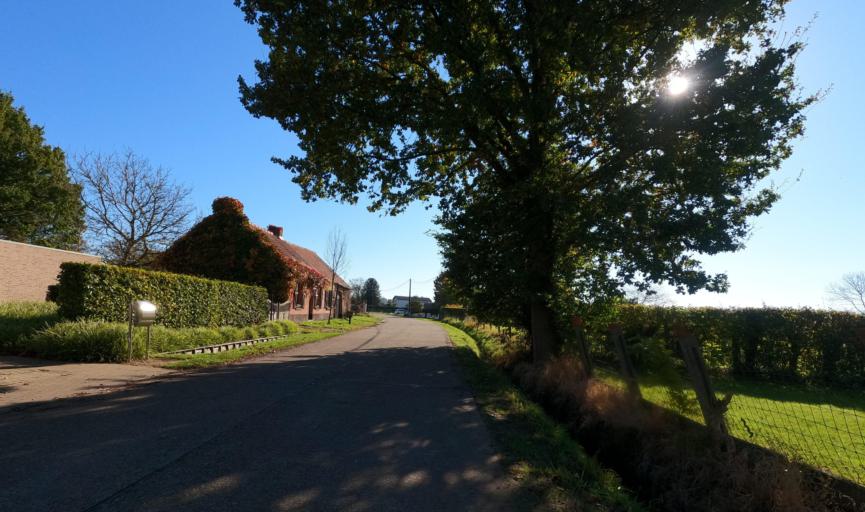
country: BE
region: Flanders
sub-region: Provincie Antwerpen
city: Herselt
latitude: 51.0876
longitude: 4.8633
